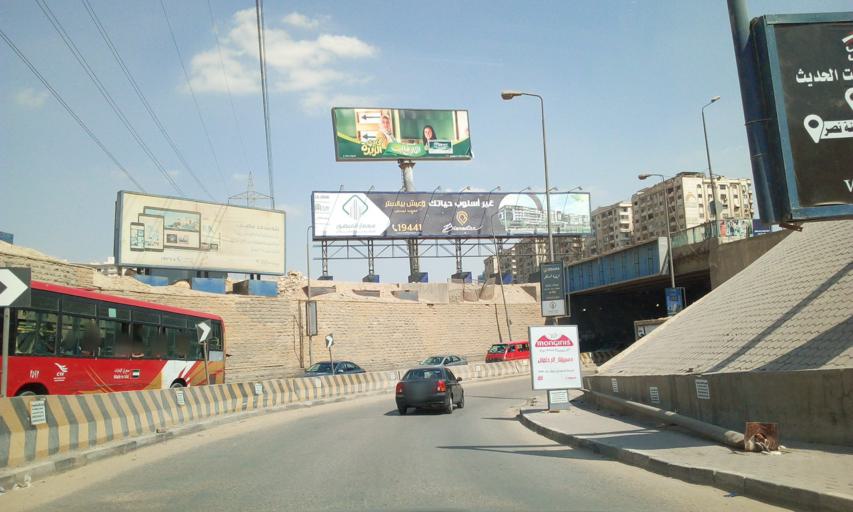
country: EG
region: Muhafazat al Qahirah
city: Cairo
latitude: 29.9846
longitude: 31.3177
